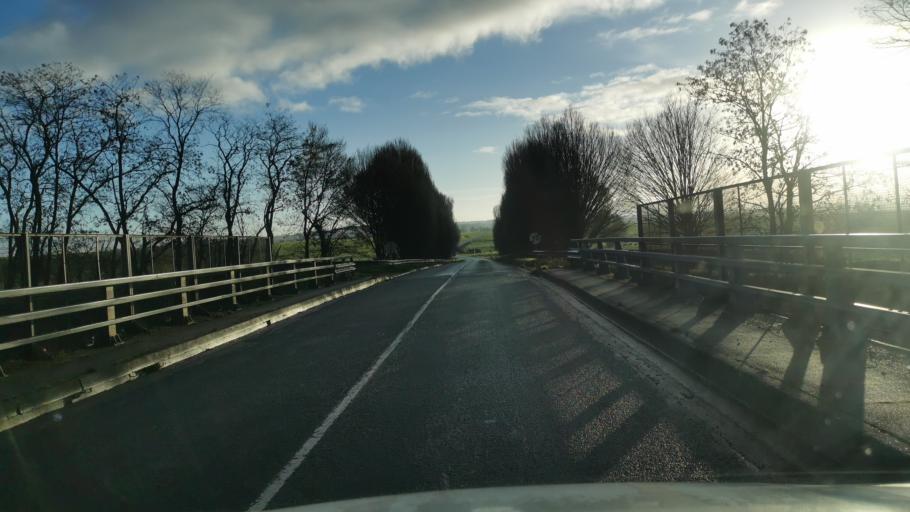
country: FR
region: Ile-de-France
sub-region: Departement des Yvelines
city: Bazainville
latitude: 48.8152
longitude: 1.6414
